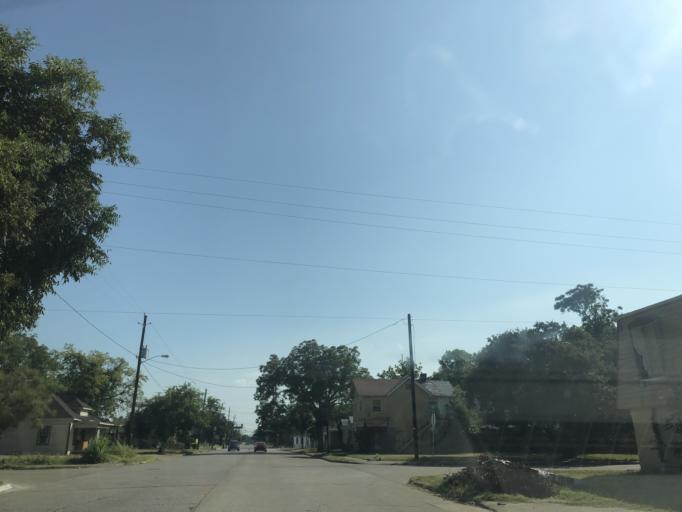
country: US
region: Texas
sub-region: Dallas County
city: Dallas
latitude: 32.7663
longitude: -96.7682
